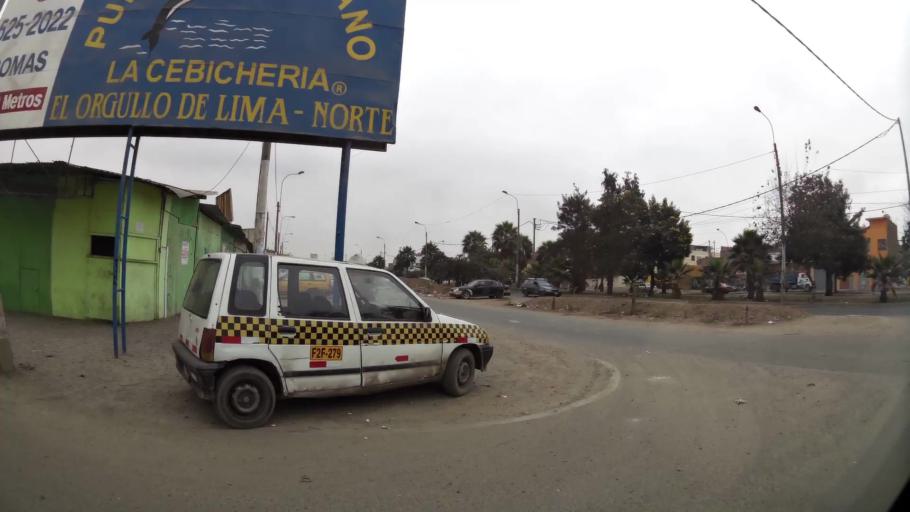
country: PE
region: Lima
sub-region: Lima
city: Independencia
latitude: -11.9574
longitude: -77.0601
